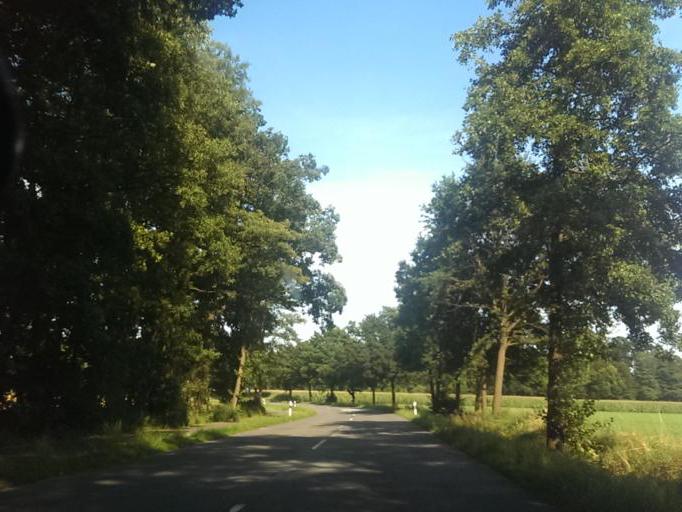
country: DE
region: North Rhine-Westphalia
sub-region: Regierungsbezirk Detmold
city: Hovelhof
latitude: 51.7880
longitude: 8.6473
